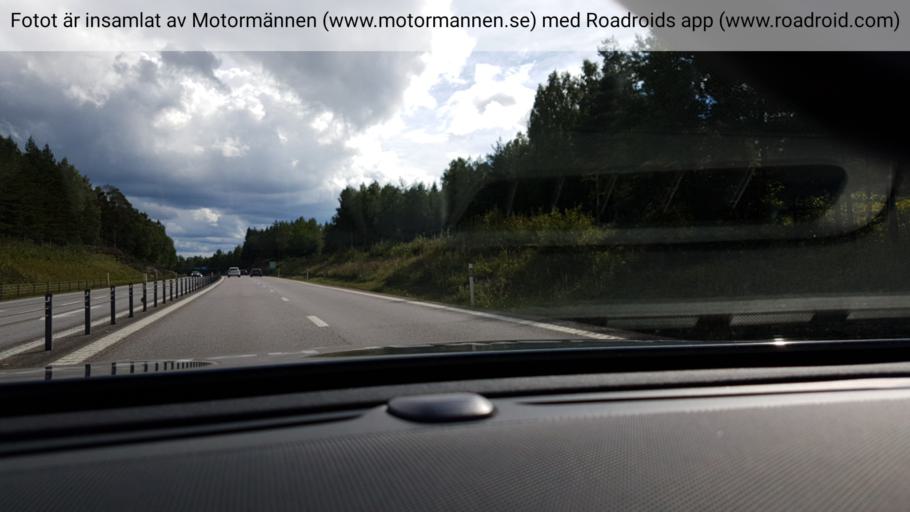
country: SE
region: Vaestra Goetaland
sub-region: Trollhattan
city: Trollhattan
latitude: 58.3301
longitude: 12.2977
